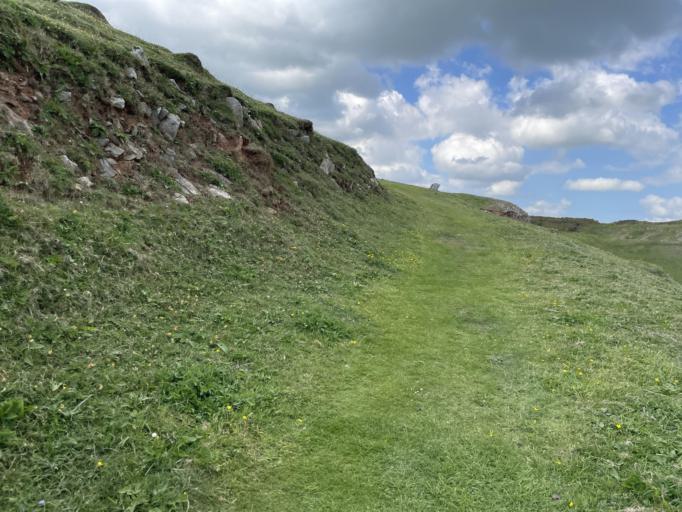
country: GB
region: Wales
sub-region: Pembrokeshire
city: Castlemartin
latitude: 51.6116
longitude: -4.9905
